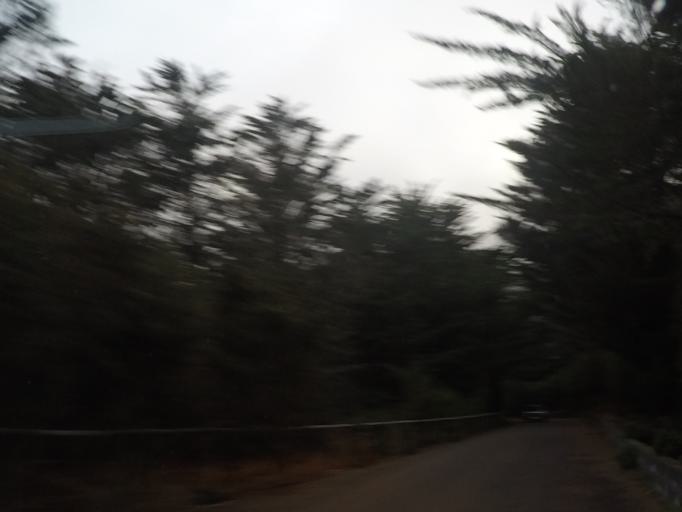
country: PT
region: Madeira
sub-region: Santa Cruz
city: Camacha
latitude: 32.7151
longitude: -16.8539
